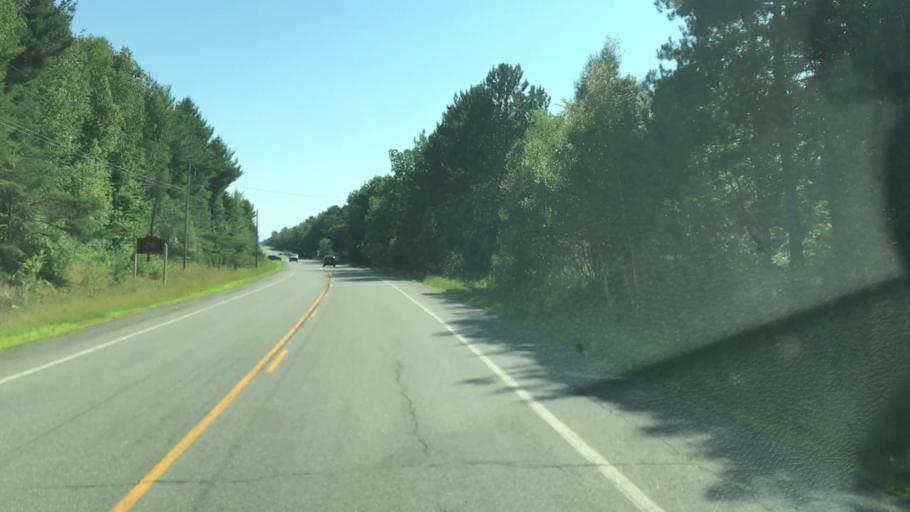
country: US
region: Maine
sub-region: Penobscot County
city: Enfield
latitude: 45.3256
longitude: -68.5943
